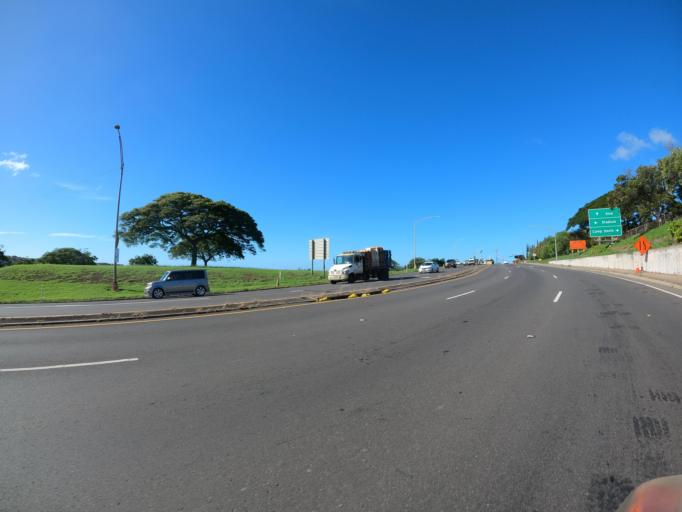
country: US
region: Hawaii
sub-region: Honolulu County
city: Halawa Heights
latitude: 21.3732
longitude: -157.9181
